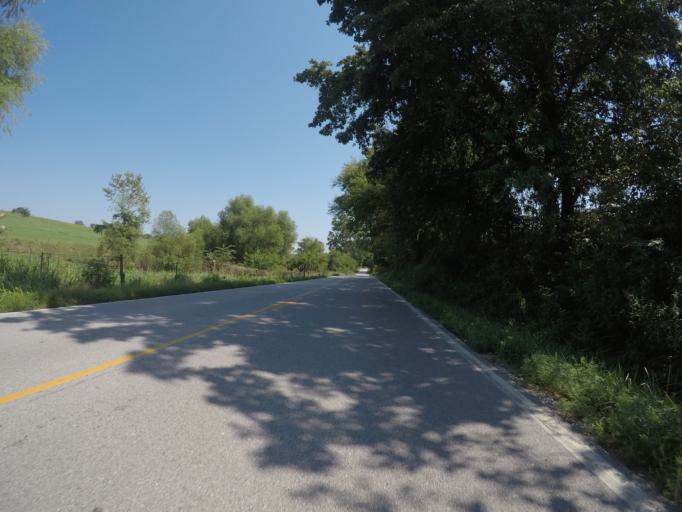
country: US
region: Kansas
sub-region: Leavenworth County
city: Lansing
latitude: 39.2067
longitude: -94.8328
